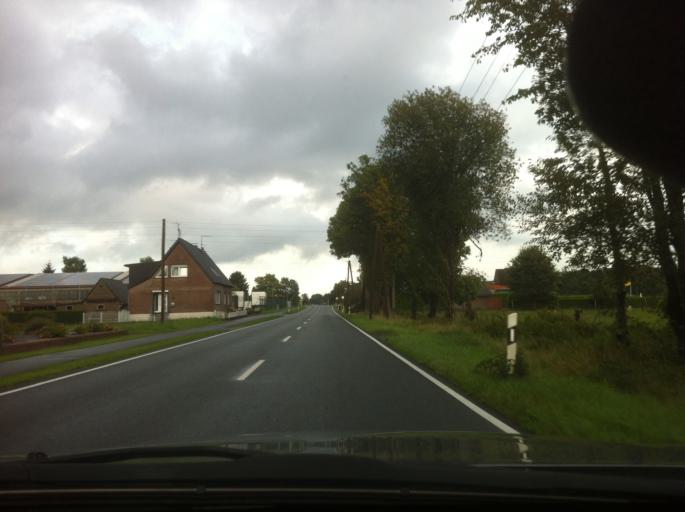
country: DE
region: North Rhine-Westphalia
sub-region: Regierungsbezirk Dusseldorf
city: Kranenburg
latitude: 51.7791
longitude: 6.0504
